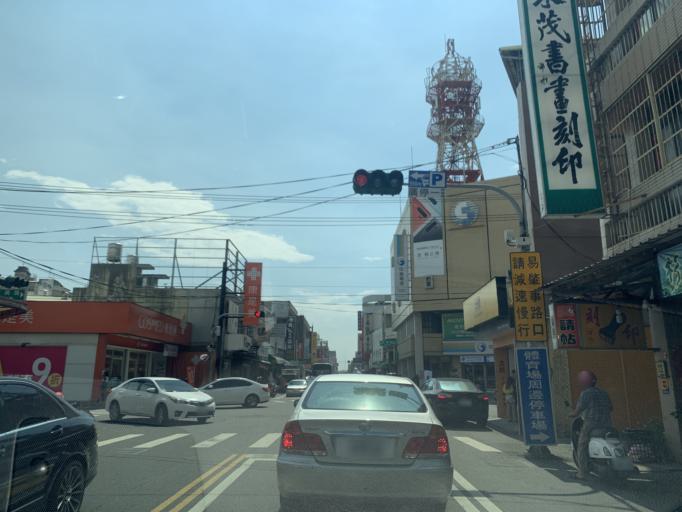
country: TW
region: Taiwan
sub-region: Changhua
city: Chang-hua
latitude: 24.0579
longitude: 120.4375
